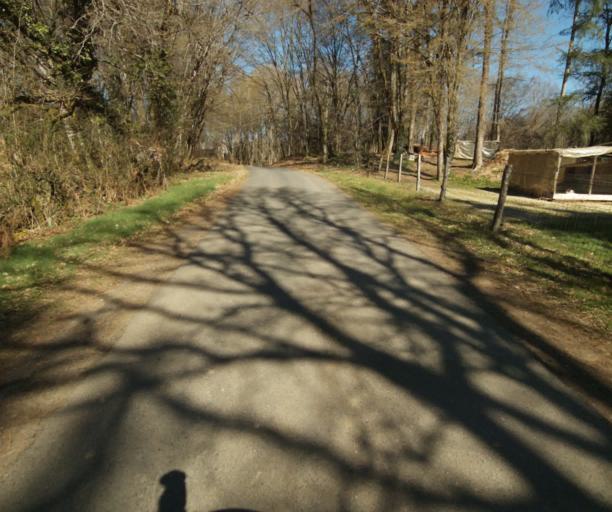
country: FR
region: Limousin
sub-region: Departement de la Correze
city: Saint-Clement
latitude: 45.3410
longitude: 1.6439
